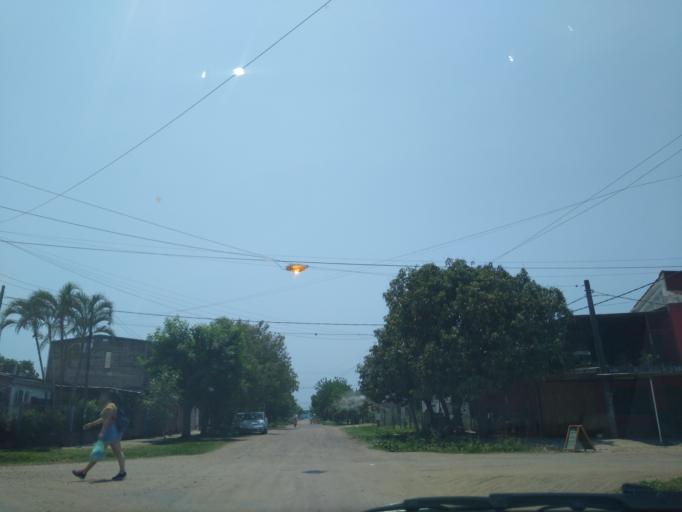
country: AR
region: Chaco
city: Barranqueras
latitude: -27.4767
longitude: -58.9328
